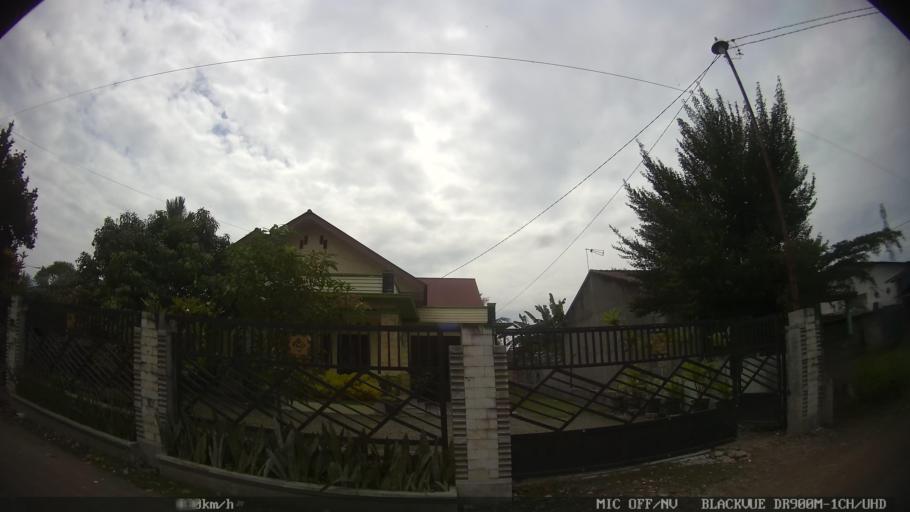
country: ID
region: North Sumatra
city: Sunggal
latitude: 3.6597
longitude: 98.5926
